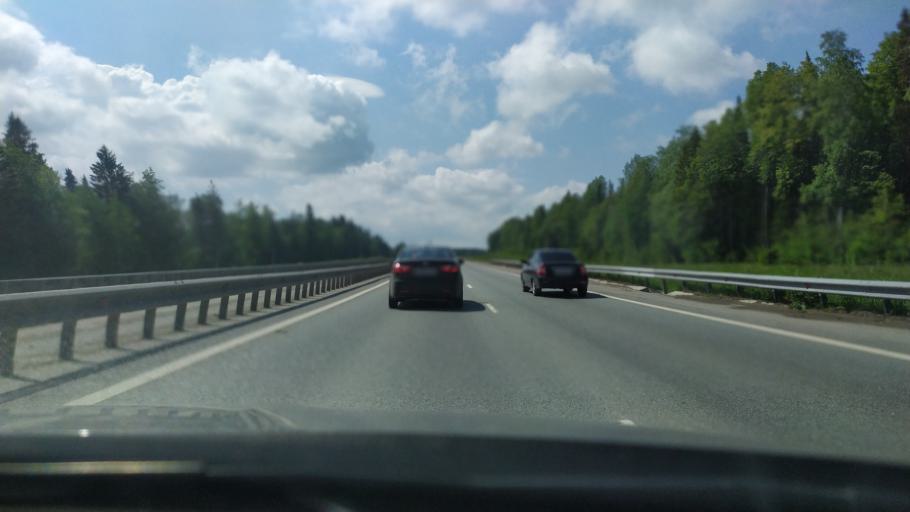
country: RU
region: Perm
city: Ferma
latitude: 58.0214
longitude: 56.4194
